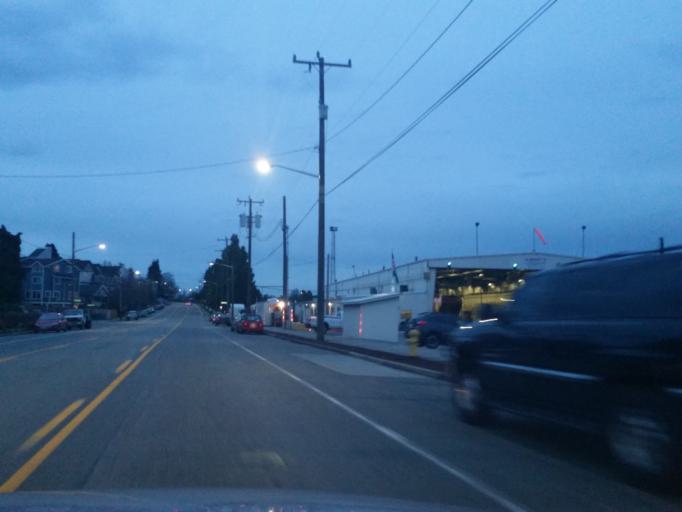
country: US
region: Washington
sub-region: King County
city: Seattle
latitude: 47.6512
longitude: -122.3824
